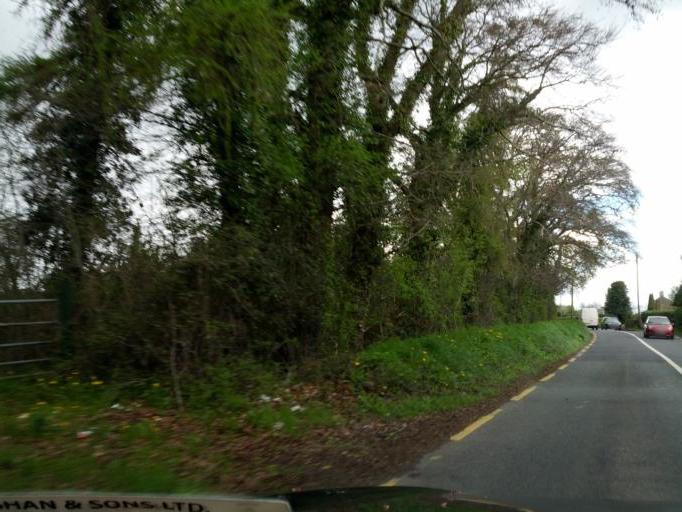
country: IE
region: Leinster
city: Lucan
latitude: 53.3778
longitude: -6.4560
